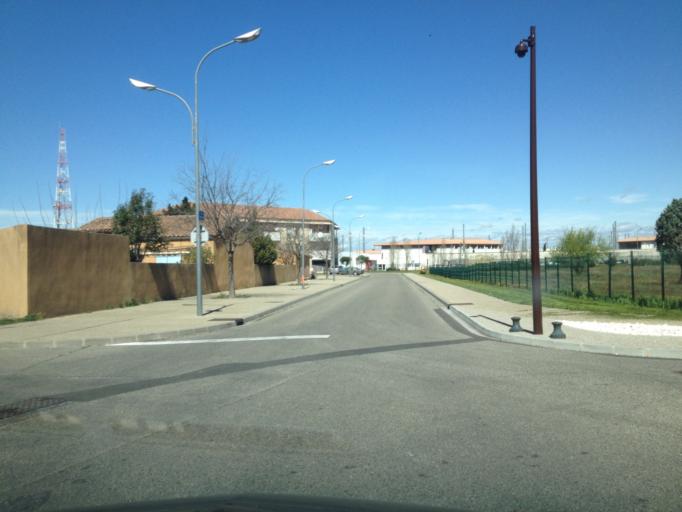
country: FR
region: Provence-Alpes-Cote d'Azur
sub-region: Departement du Vaucluse
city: Le Pontet
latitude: 43.9662
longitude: 4.8606
